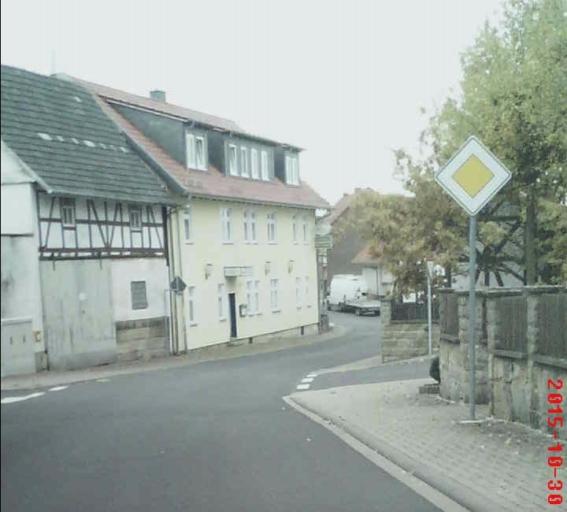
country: DE
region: Thuringia
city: Krombach
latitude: 51.3194
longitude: 10.1379
